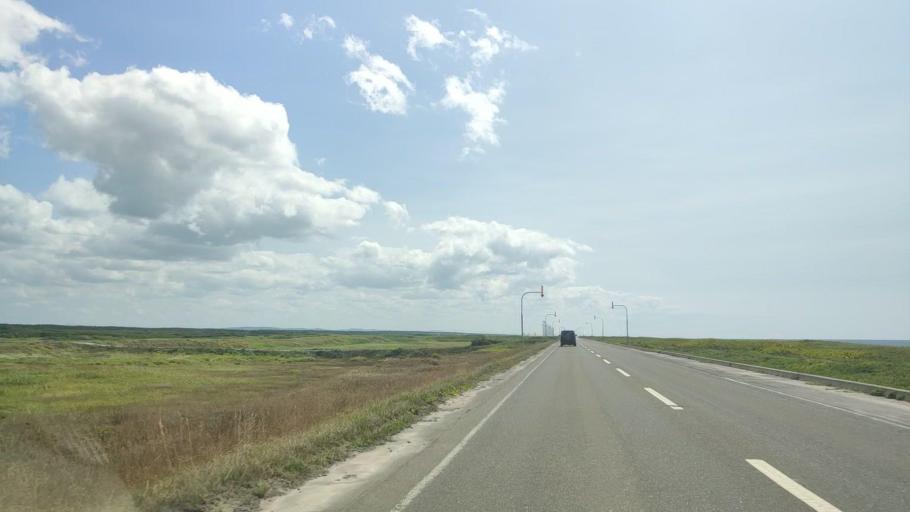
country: JP
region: Hokkaido
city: Makubetsu
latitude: 45.0188
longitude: 141.6723
